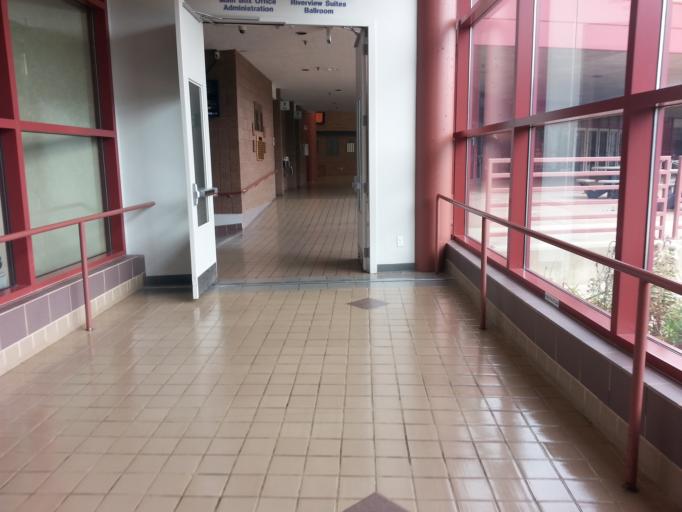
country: US
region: Minnesota
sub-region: Olmsted County
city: Rochester
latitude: 44.0222
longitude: -92.4596
